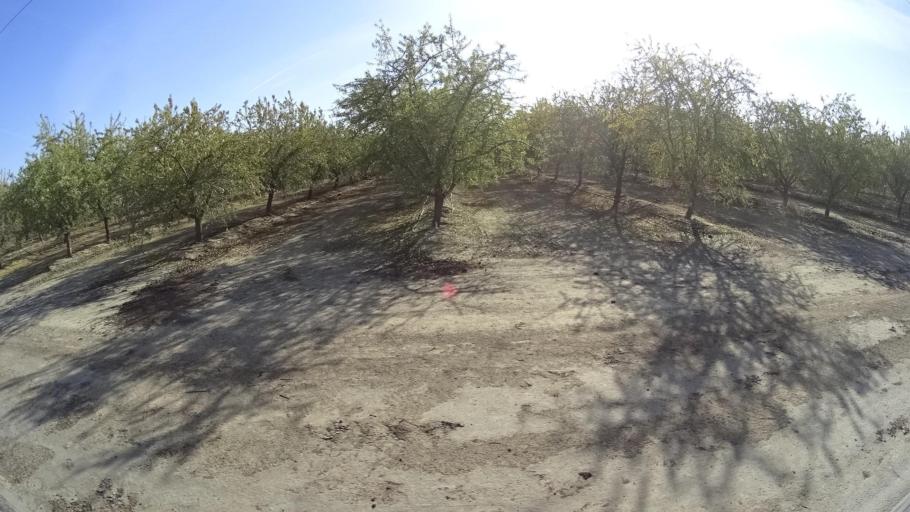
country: US
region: California
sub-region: Kern County
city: Wasco
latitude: 35.7032
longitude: -119.3562
